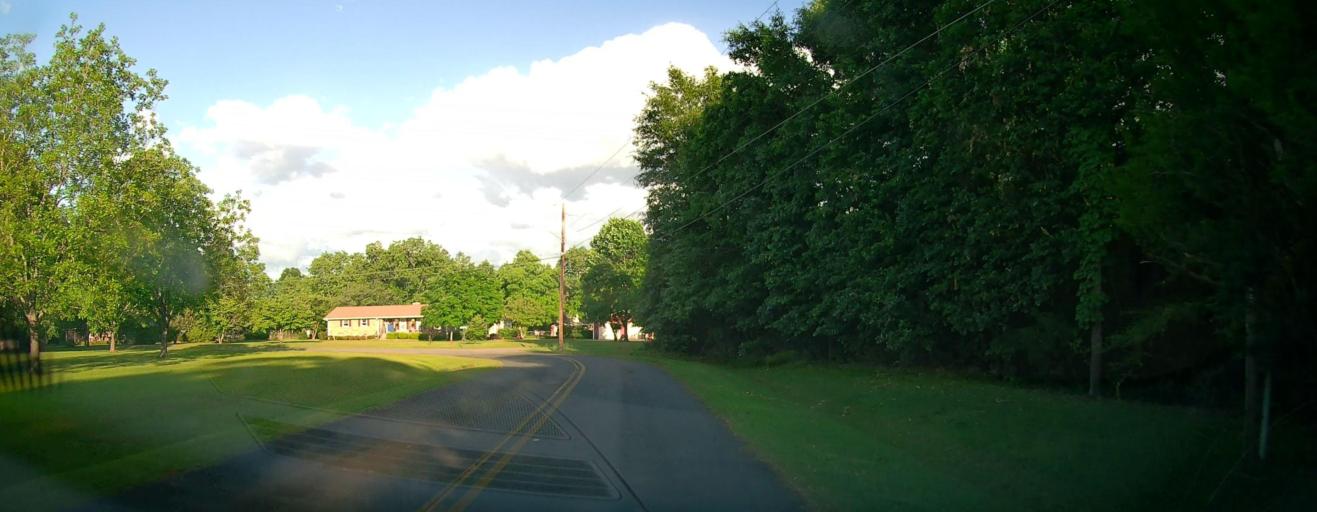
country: US
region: Georgia
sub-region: Peach County
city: Byron
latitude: 32.6426
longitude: -83.7506
